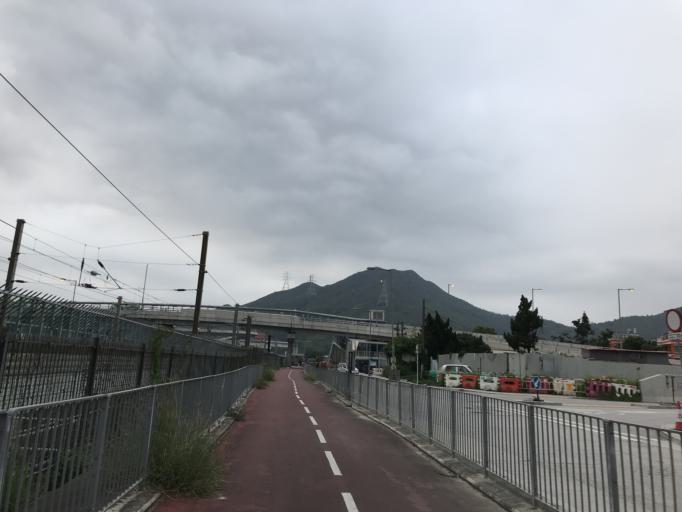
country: HK
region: Tai Po
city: Tai Po
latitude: 22.4739
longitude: 114.1542
